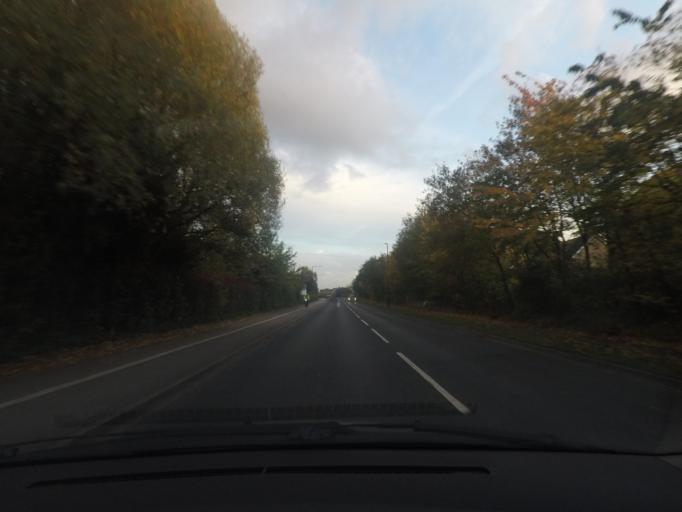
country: GB
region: England
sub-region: City of York
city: Skelton
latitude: 53.9890
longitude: -1.1048
